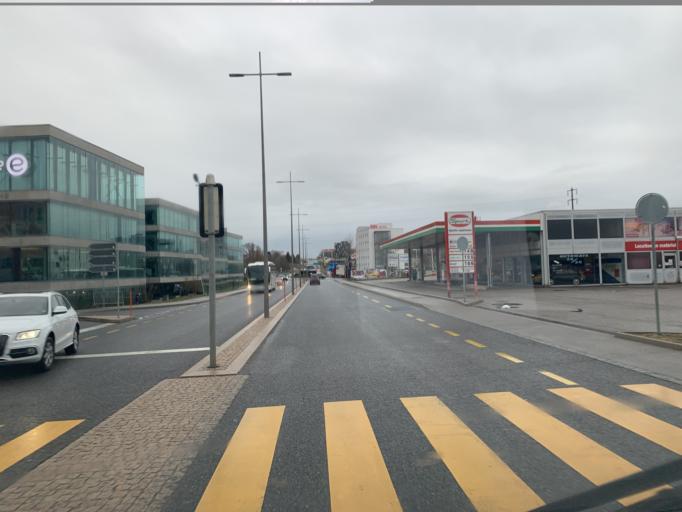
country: CH
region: Fribourg
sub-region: Sarine District
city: Fribourg
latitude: 46.8221
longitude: 7.1512
